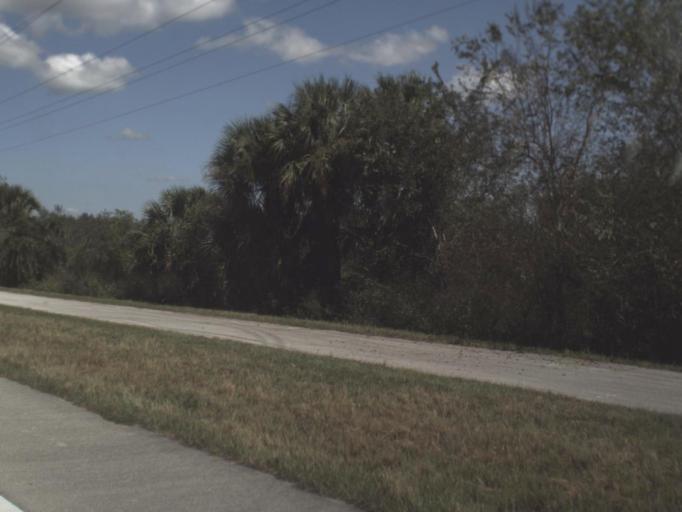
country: US
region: Florida
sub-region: Glades County
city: Moore Haven
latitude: 26.9561
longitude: -81.1221
